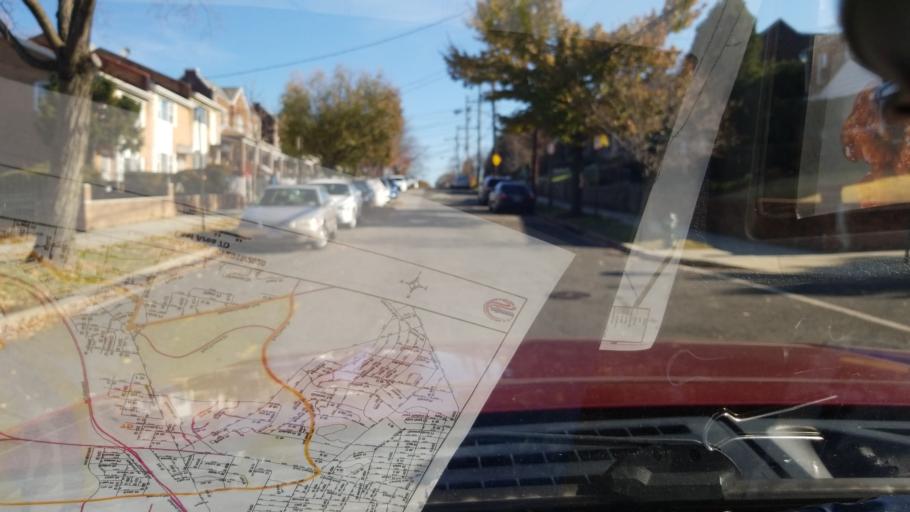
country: US
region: Maryland
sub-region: Prince George's County
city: Capitol Heights
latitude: 38.8919
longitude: -76.9505
